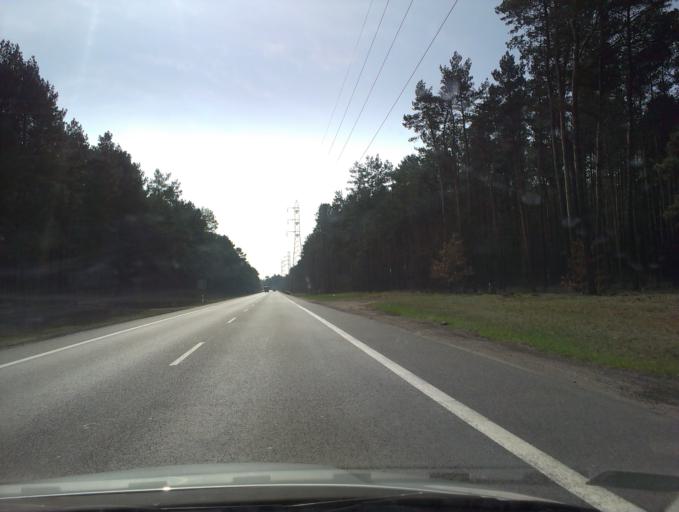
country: PL
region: Greater Poland Voivodeship
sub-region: Powiat pilski
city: Pila
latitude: 53.1575
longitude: 16.7874
